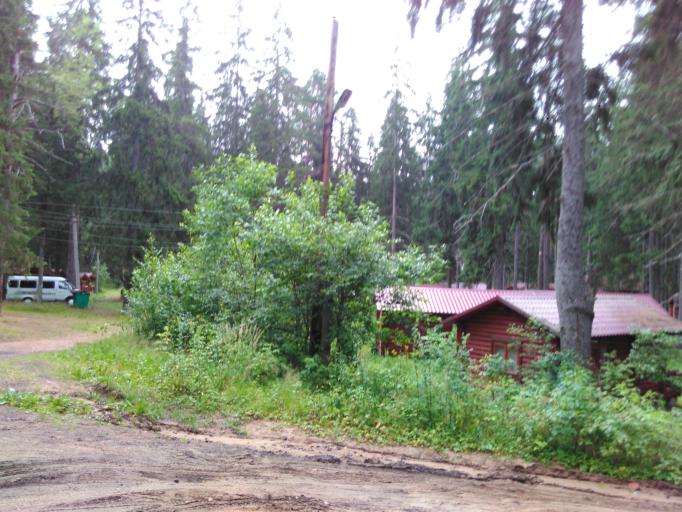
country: RU
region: Tverskaya
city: Ostashkov
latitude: 57.2058
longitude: 32.9804
